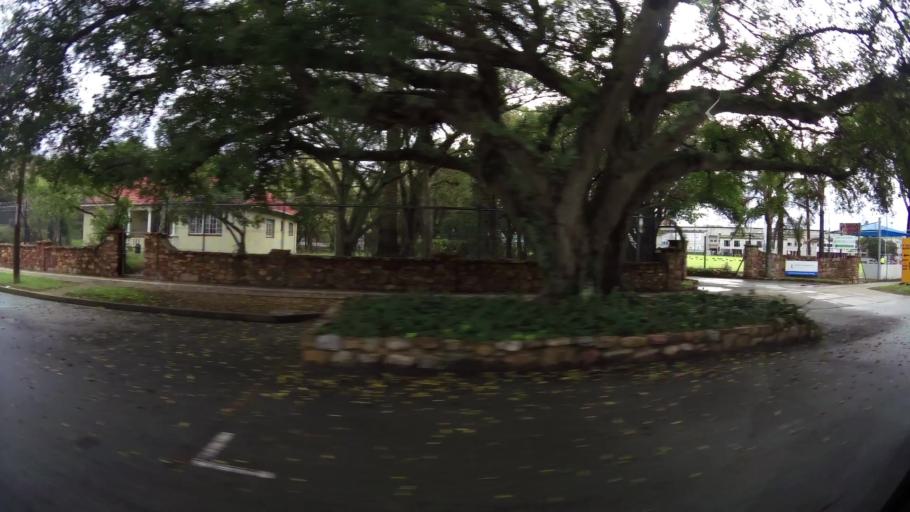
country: ZA
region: Eastern Cape
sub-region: Nelson Mandela Bay Metropolitan Municipality
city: Port Elizabeth
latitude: -33.9680
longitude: 25.6080
